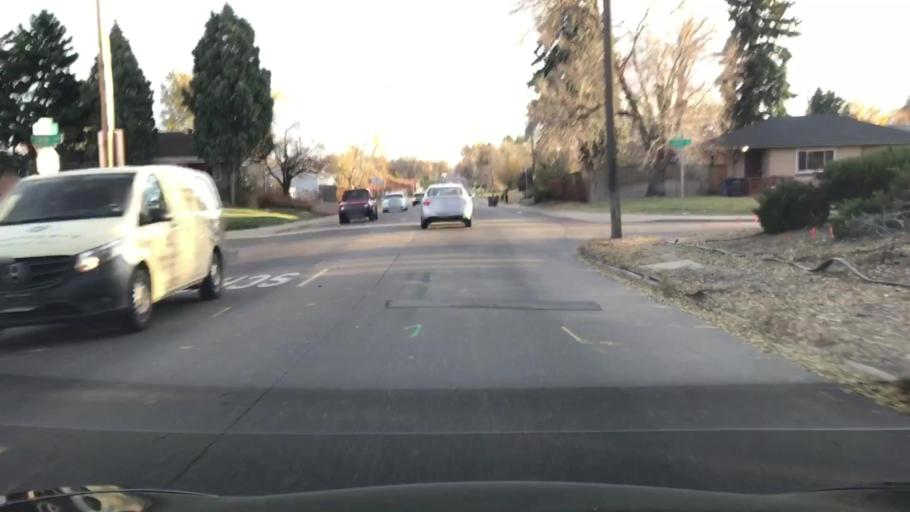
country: US
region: Colorado
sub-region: Arapahoe County
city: Glendale
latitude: 39.7359
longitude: -104.9035
